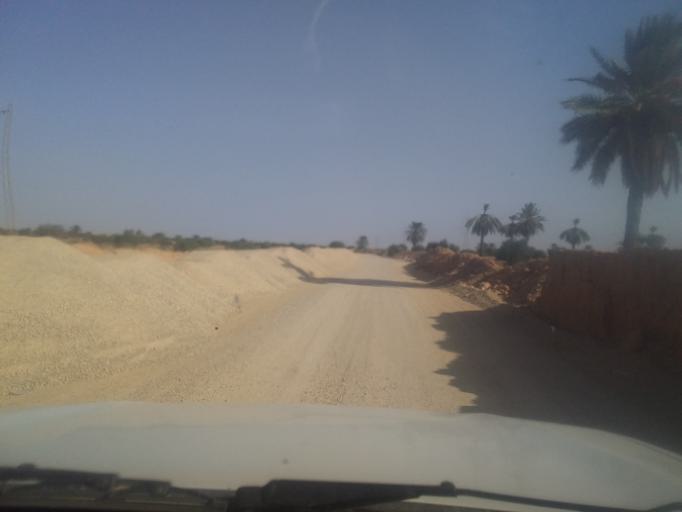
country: TN
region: Qabis
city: Matmata
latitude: 33.5893
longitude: 10.2674
